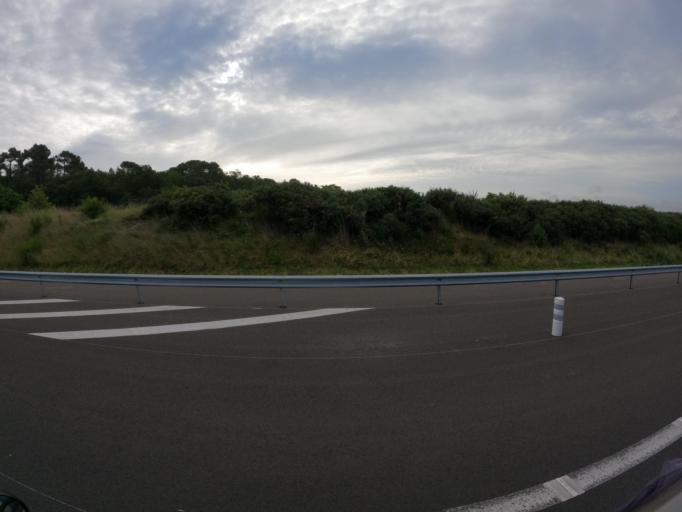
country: FR
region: Centre
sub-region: Departement d'Indre-et-Loire
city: Restigne
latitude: 47.2849
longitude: 0.2816
